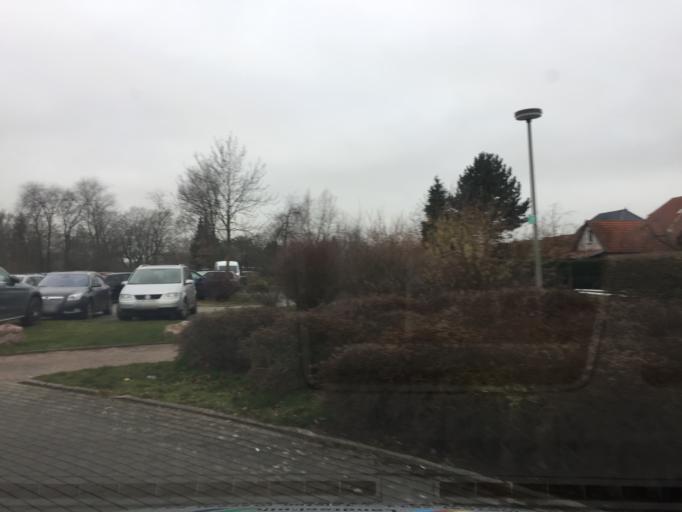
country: DE
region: Lower Saxony
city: Stadthagen
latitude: 52.3225
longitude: 9.1893
